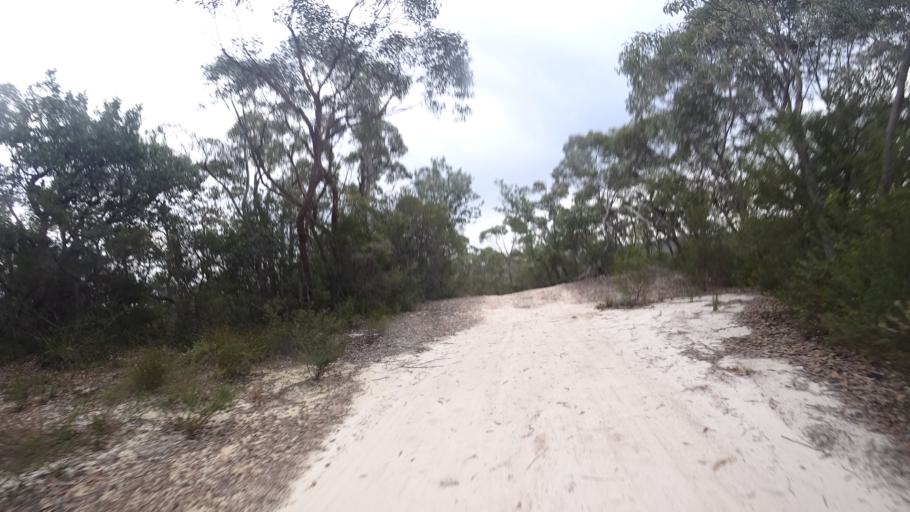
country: AU
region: New South Wales
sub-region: Warringah
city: Davidson
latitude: -33.6984
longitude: 151.1994
